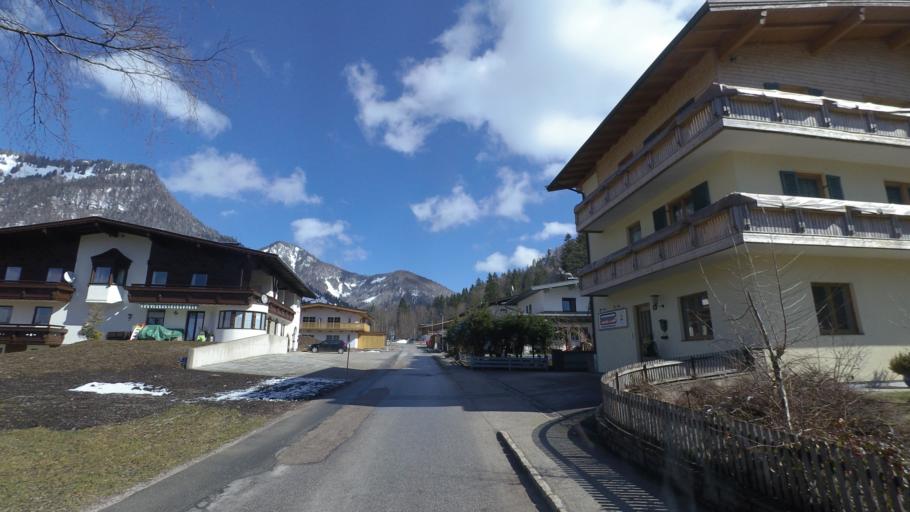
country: AT
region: Tyrol
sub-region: Politischer Bezirk Kufstein
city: Walchsee
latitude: 47.6586
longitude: 12.3215
